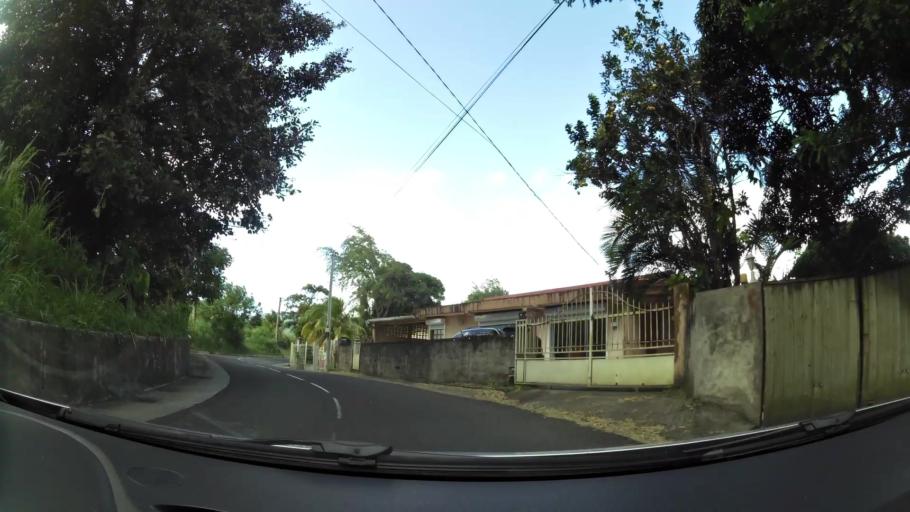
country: MQ
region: Martinique
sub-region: Martinique
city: Fort-de-France
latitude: 14.6516
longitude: -61.0862
